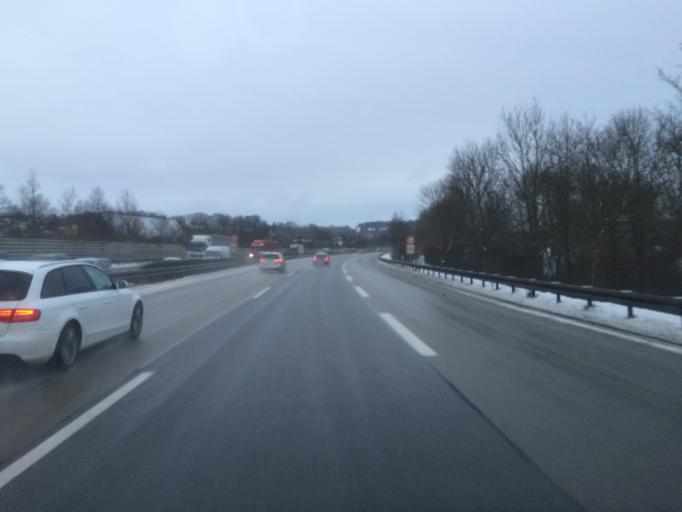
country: DE
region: Bavaria
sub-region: Upper Palatinate
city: Lappersdorf
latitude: 49.0475
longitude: 12.0939
